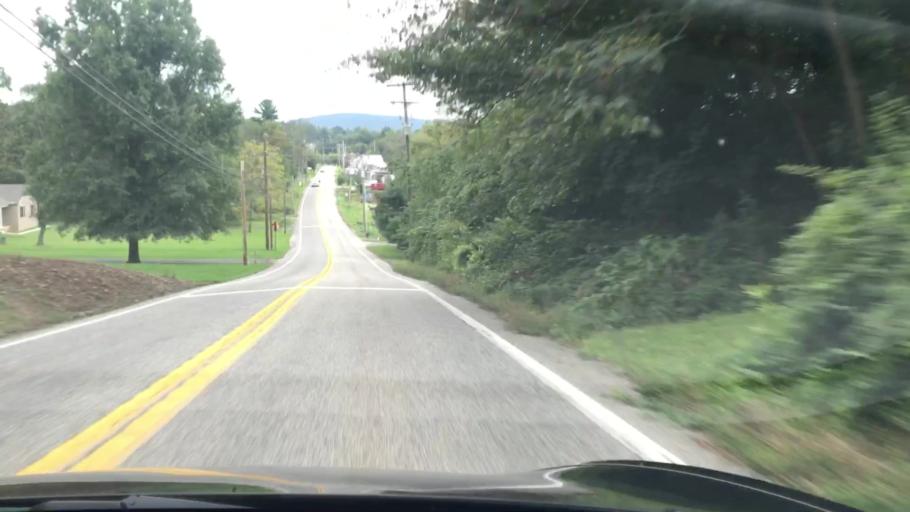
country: US
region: Pennsylvania
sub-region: Cumberland County
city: Shiremanstown
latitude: 40.1489
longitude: -76.9665
